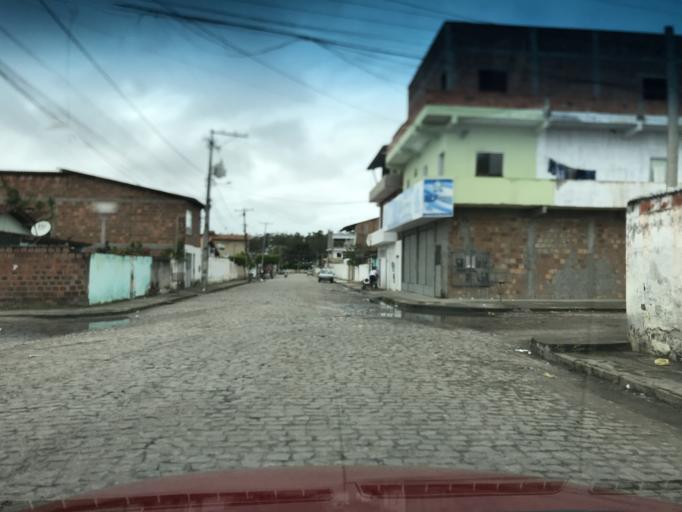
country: BR
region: Bahia
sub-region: Cruz Das Almas
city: Cruz das Almas
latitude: -12.6603
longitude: -39.1034
